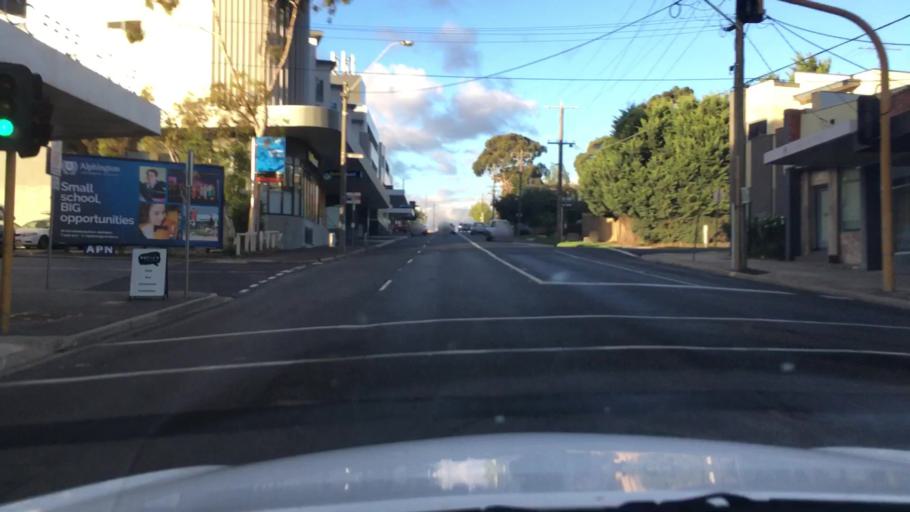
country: AU
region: Victoria
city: Alphington
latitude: -37.7753
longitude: 145.0391
